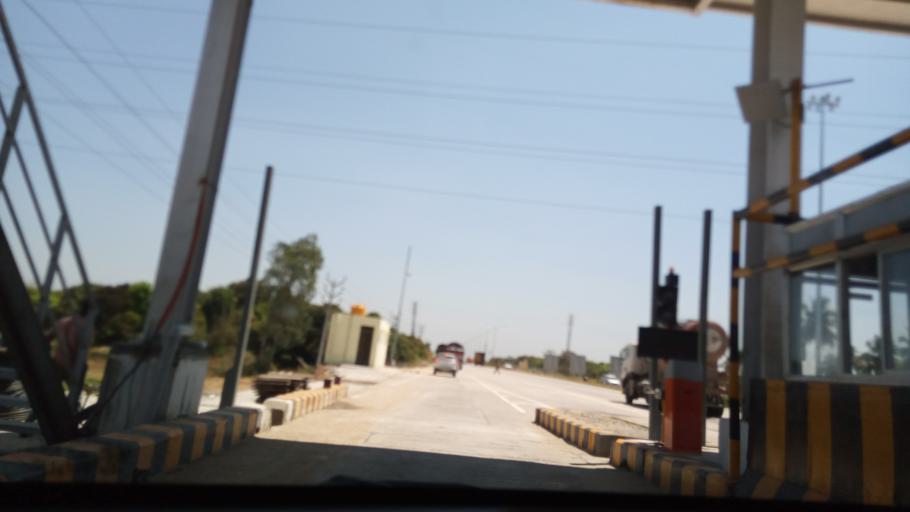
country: IN
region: Andhra Pradesh
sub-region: Chittoor
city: Chittoor
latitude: 13.1950
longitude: 79.0184
